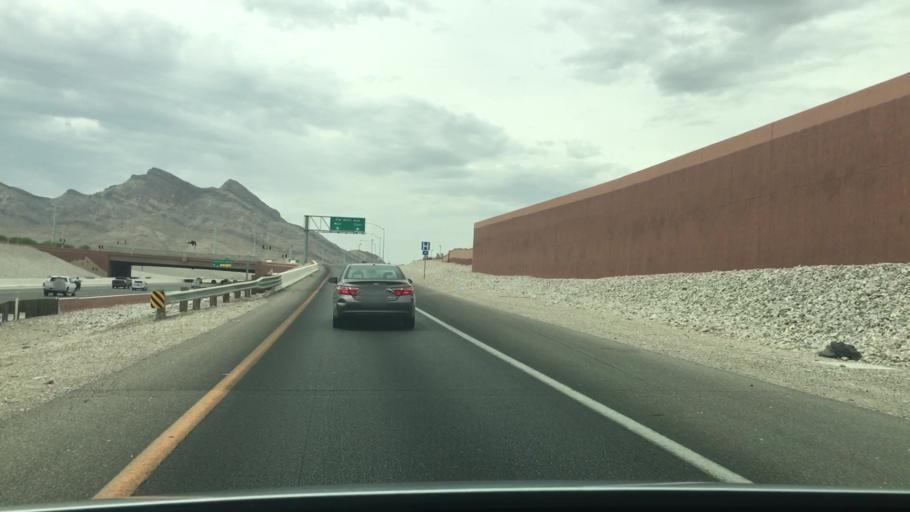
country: US
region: Nevada
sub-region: Clark County
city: Summerlin South
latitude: 36.1785
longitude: -115.3395
